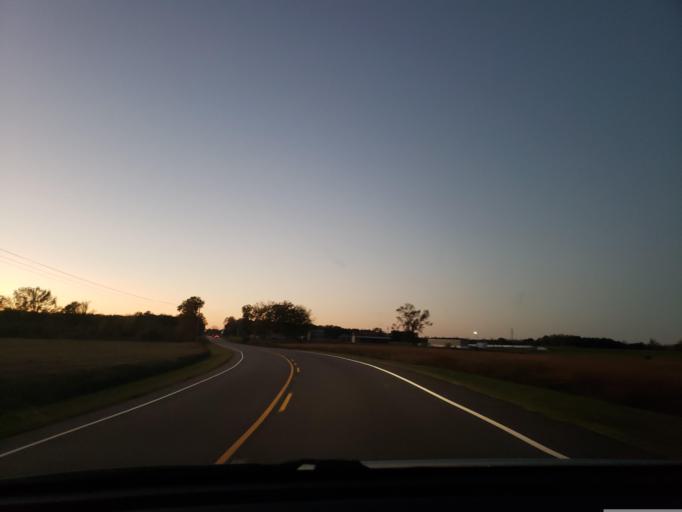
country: US
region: North Carolina
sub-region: Duplin County
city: Kenansville
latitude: 34.8981
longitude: -77.9112
